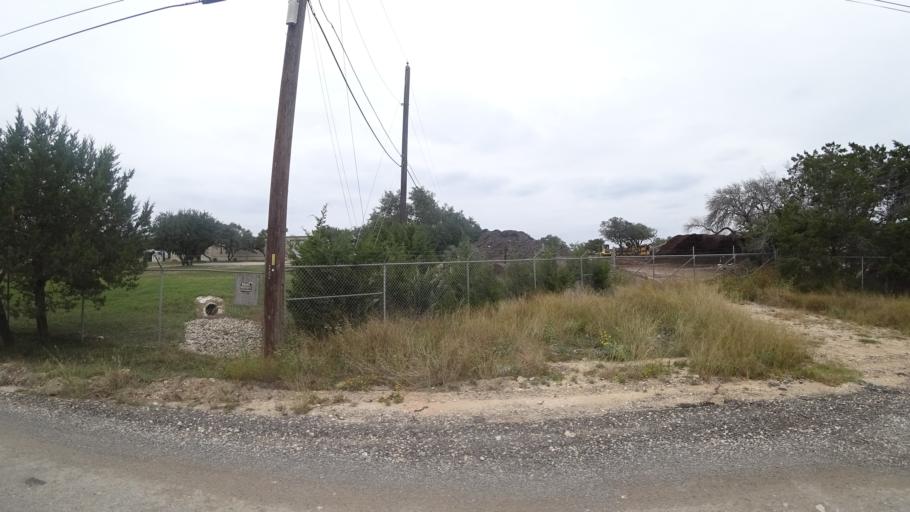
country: US
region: Texas
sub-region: Travis County
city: Hudson Bend
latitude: 30.3815
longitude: -97.9394
